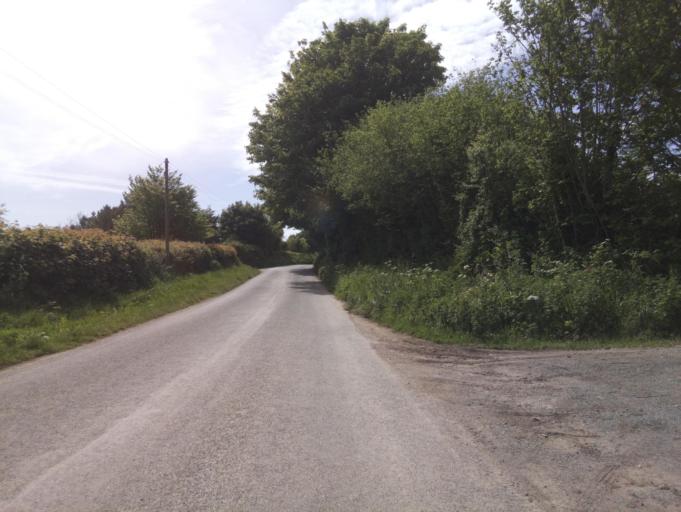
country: GB
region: England
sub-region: Devon
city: Kingsbridge
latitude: 50.3604
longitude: -3.7443
